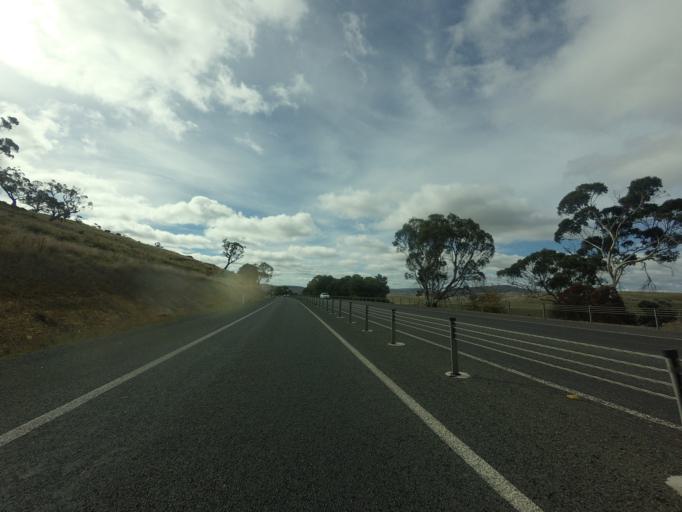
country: AU
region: Tasmania
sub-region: Brighton
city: Bridgewater
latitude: -42.3976
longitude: 147.2734
